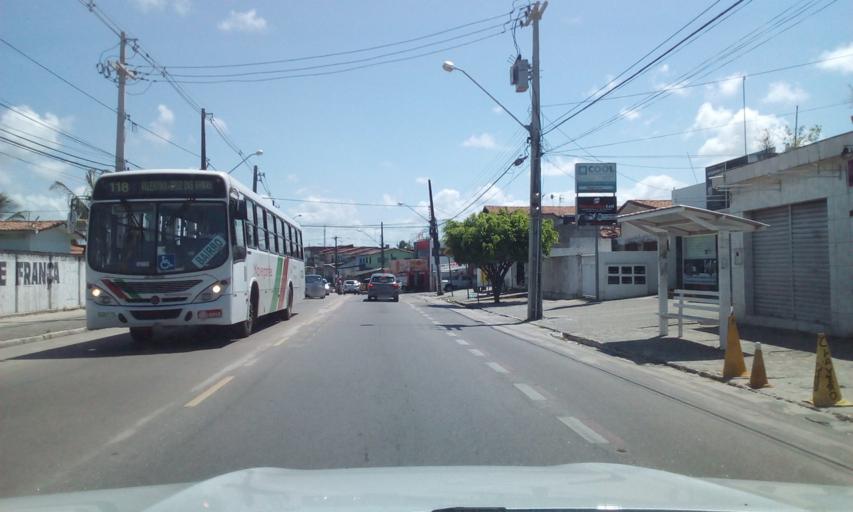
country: BR
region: Paraiba
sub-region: Conde
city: Conde
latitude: -7.2047
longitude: -34.8480
